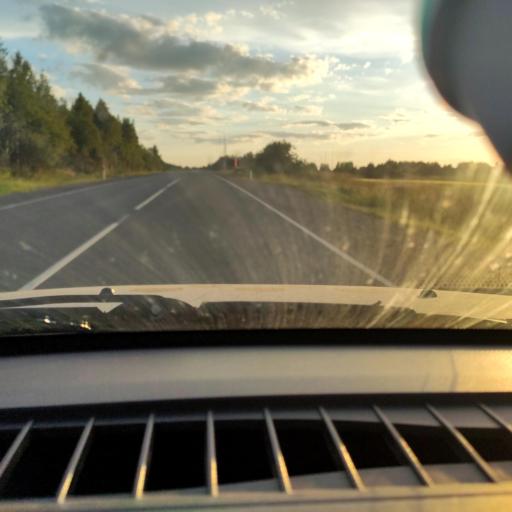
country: RU
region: Kirov
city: Kotel'nich
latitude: 58.3292
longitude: 48.2745
